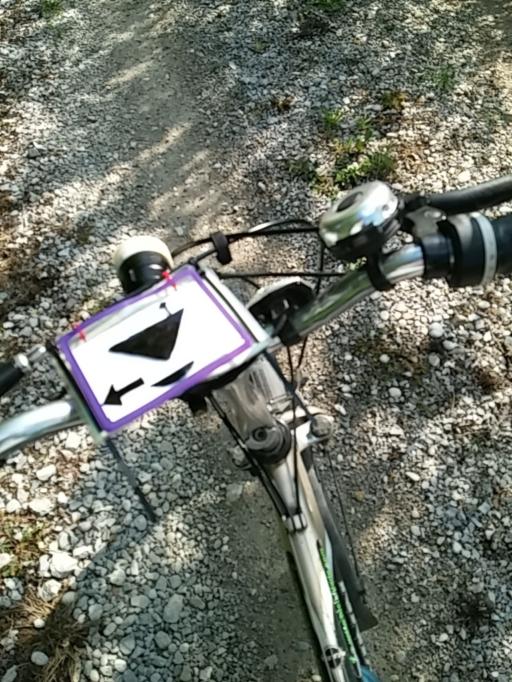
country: HR
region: Grad Zagreb
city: Stenjevec
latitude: 45.8357
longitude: 15.9189
